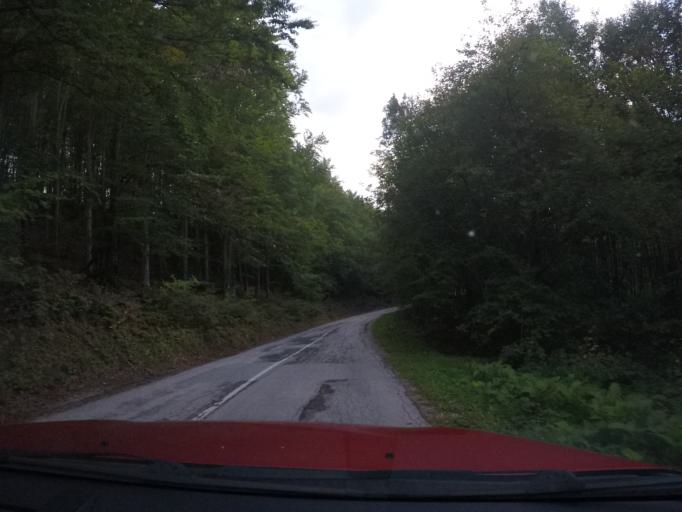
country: SK
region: Kosicky
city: Medzev
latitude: 48.6302
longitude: 20.7223
